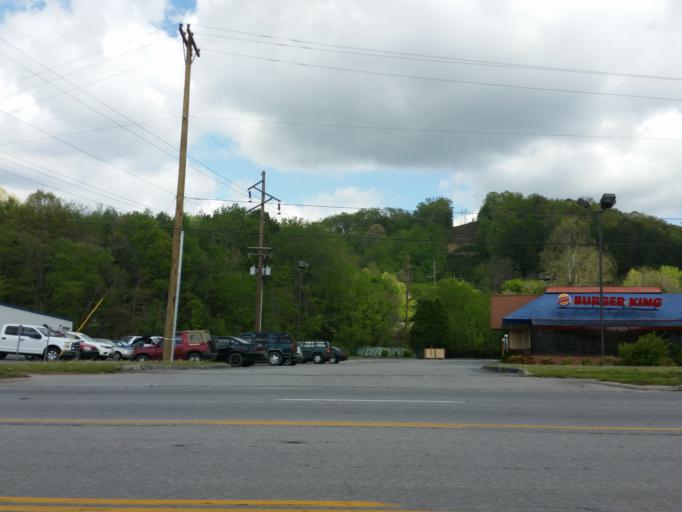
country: US
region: Kentucky
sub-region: Bell County
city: Middlesboro
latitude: 36.6106
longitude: -83.7023
